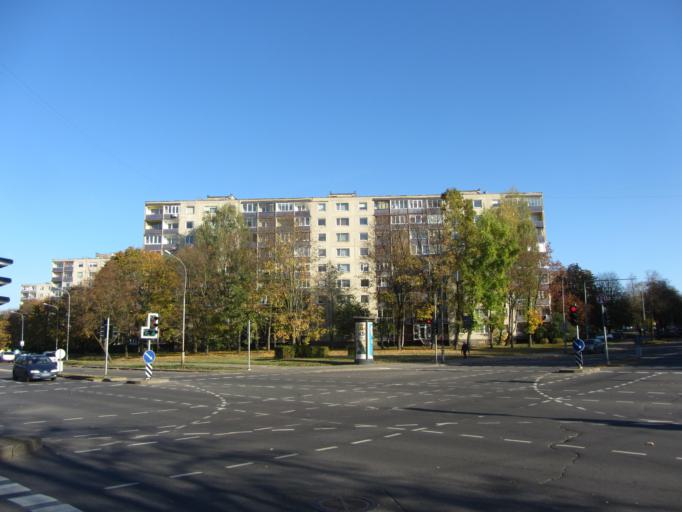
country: LT
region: Vilnius County
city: Lazdynai
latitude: 54.6740
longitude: 25.2013
